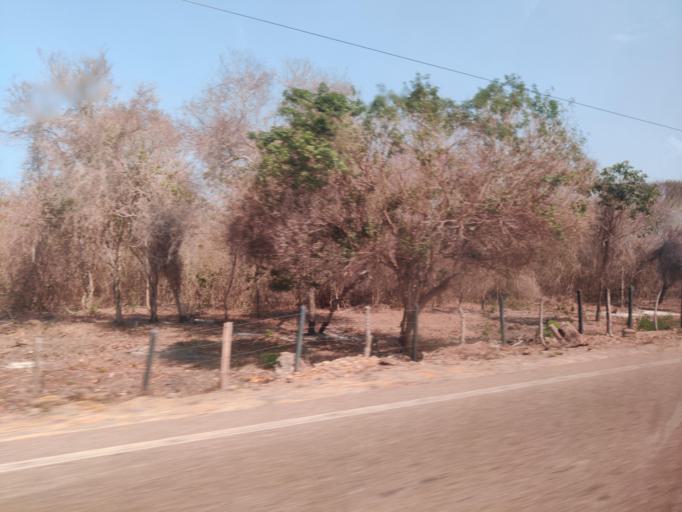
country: CO
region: Bolivar
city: Turbana
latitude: 10.2149
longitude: -75.5949
